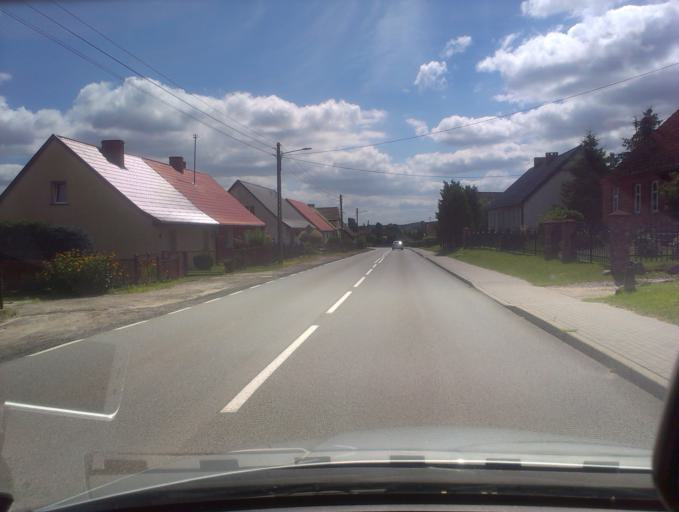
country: PL
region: West Pomeranian Voivodeship
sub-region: Powiat szczecinecki
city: Szczecinek
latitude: 53.7353
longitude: 16.8025
